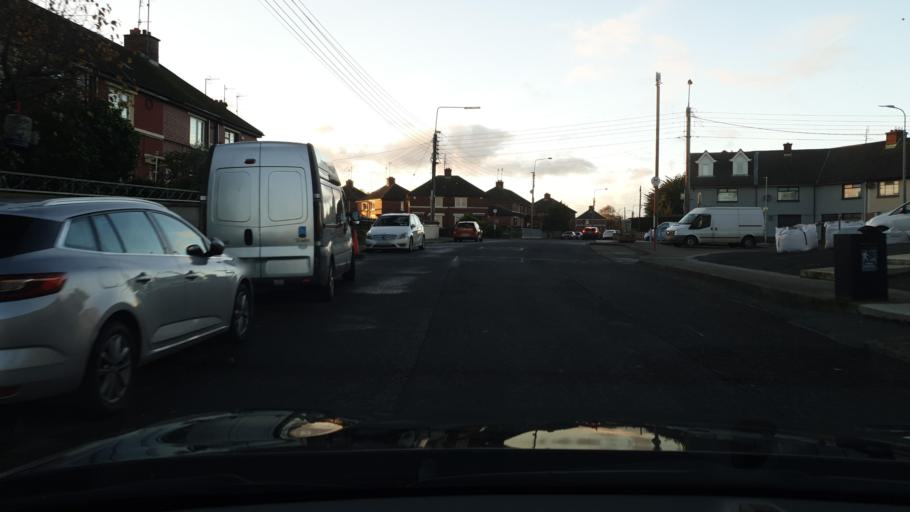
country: IE
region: Leinster
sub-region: Lu
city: Drogheda
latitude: 53.7213
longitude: -6.3444
